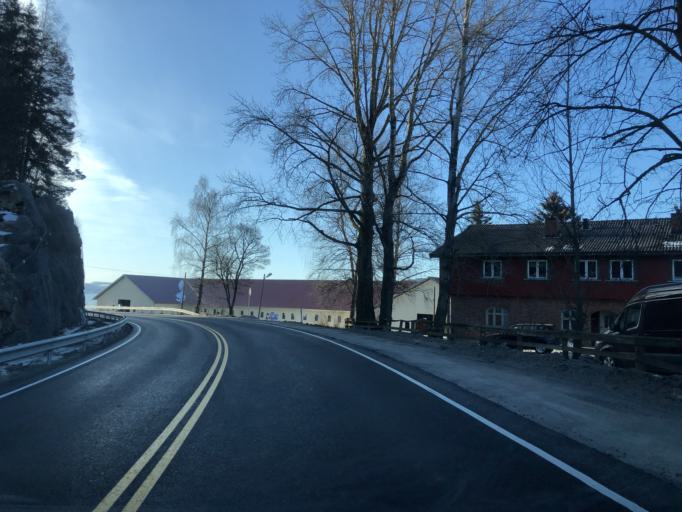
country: NO
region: Hedmark
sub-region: Ringsaker
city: Moelv
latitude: 60.9098
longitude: 10.7055
